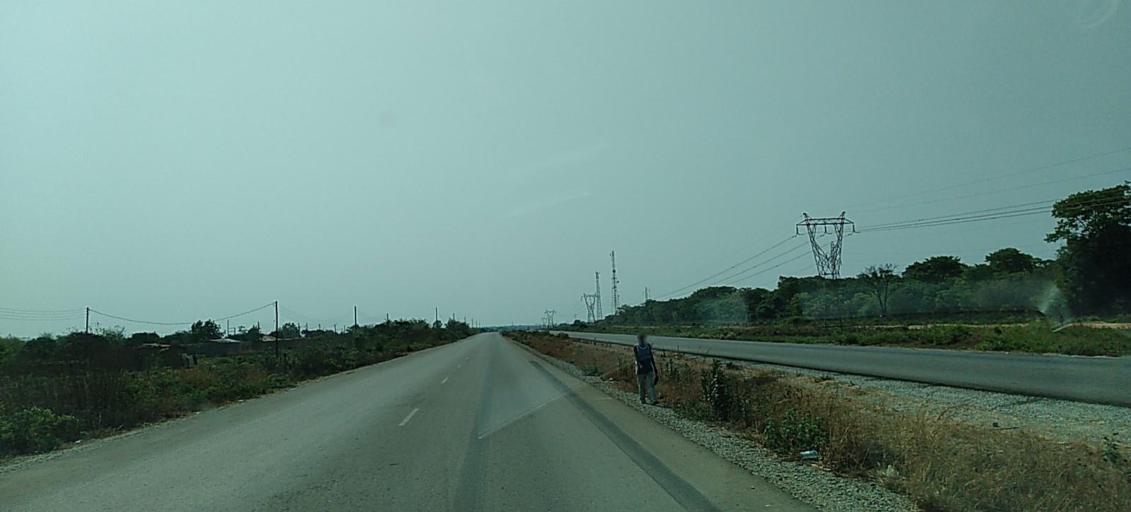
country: ZM
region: Copperbelt
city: Chingola
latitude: -12.5917
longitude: 27.9496
